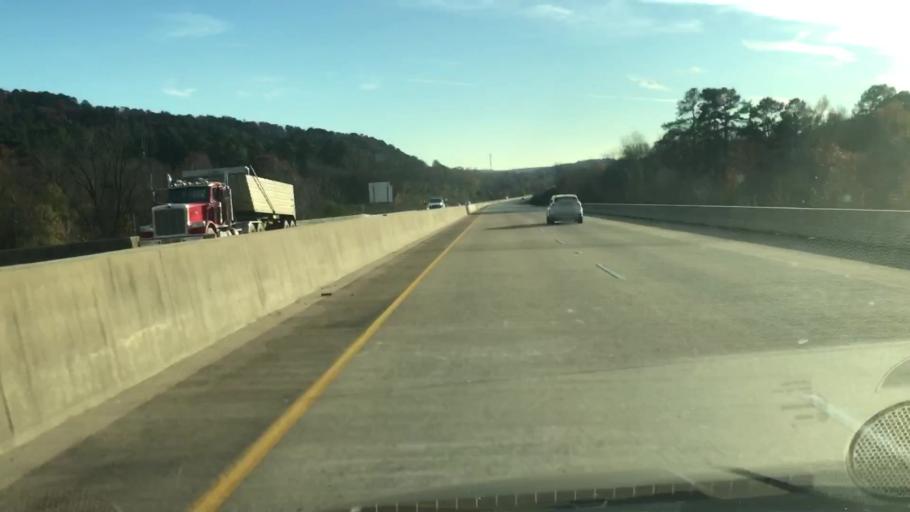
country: US
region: Arkansas
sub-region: Garland County
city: Hot Springs
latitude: 34.4856
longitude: -92.9812
